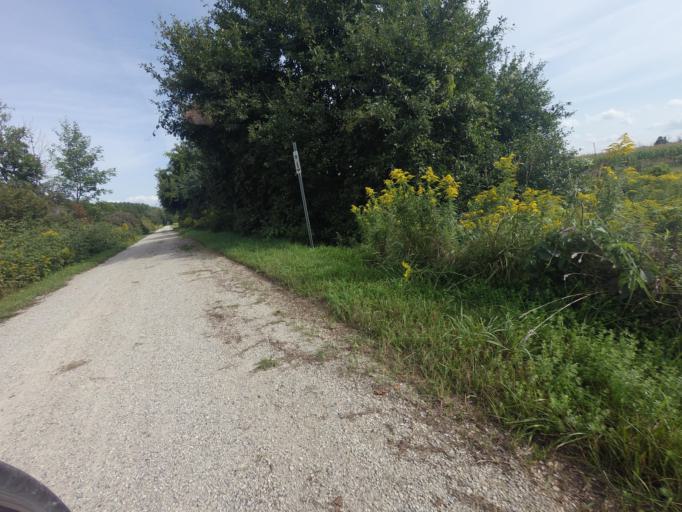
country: CA
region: Ontario
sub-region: Wellington County
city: Guelph
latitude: 43.5792
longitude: -80.3889
